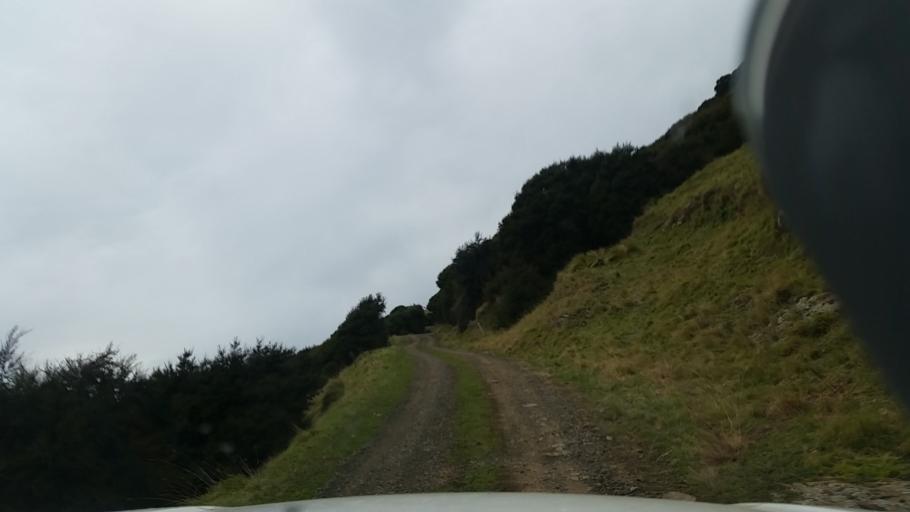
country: NZ
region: Canterbury
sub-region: Christchurch City
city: Christchurch
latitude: -43.8575
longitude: 173.0388
